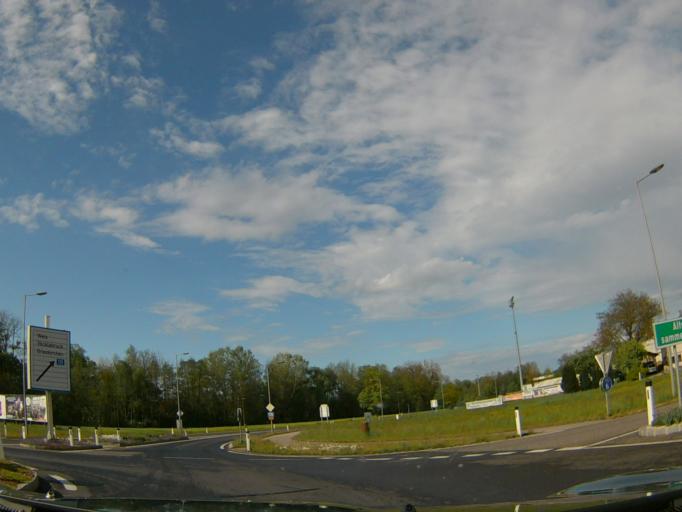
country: AT
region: Upper Austria
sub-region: Politischer Bezirk Vocklabruck
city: Schwanenstadt
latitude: 48.0480
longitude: 13.7806
